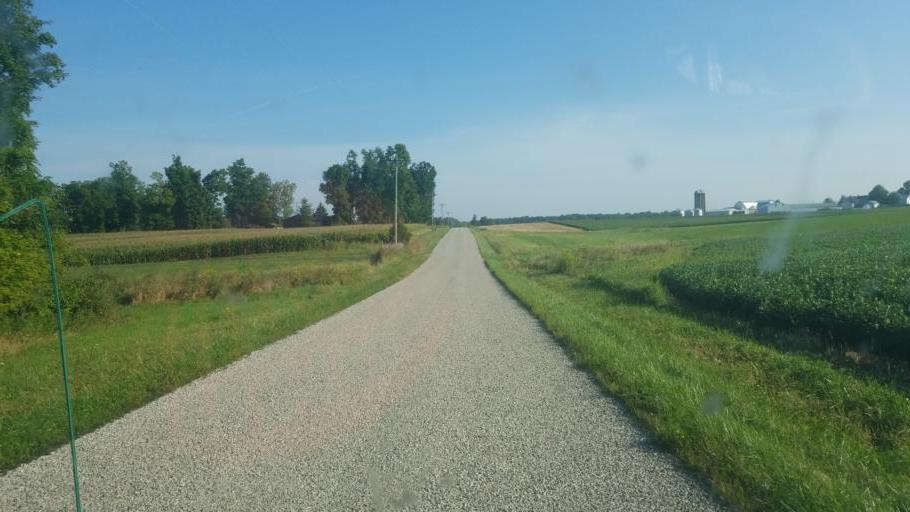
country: US
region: Ohio
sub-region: Ashland County
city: Ashland
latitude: 40.9511
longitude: -82.3398
